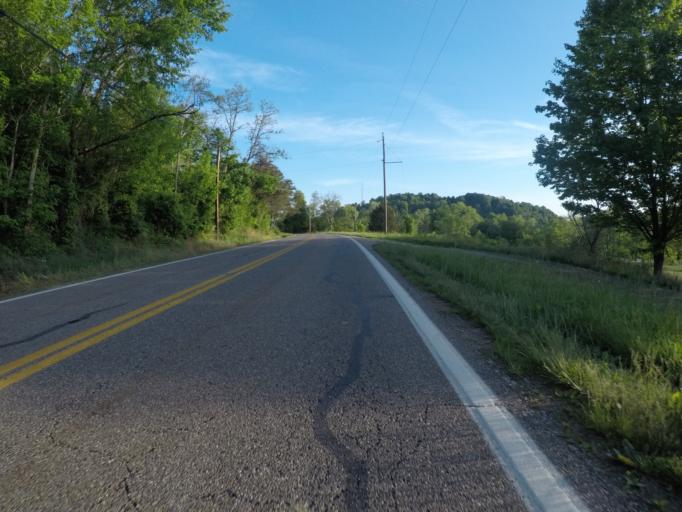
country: US
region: West Virginia
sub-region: Cabell County
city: Huntington
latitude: 38.5070
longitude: -82.4775
